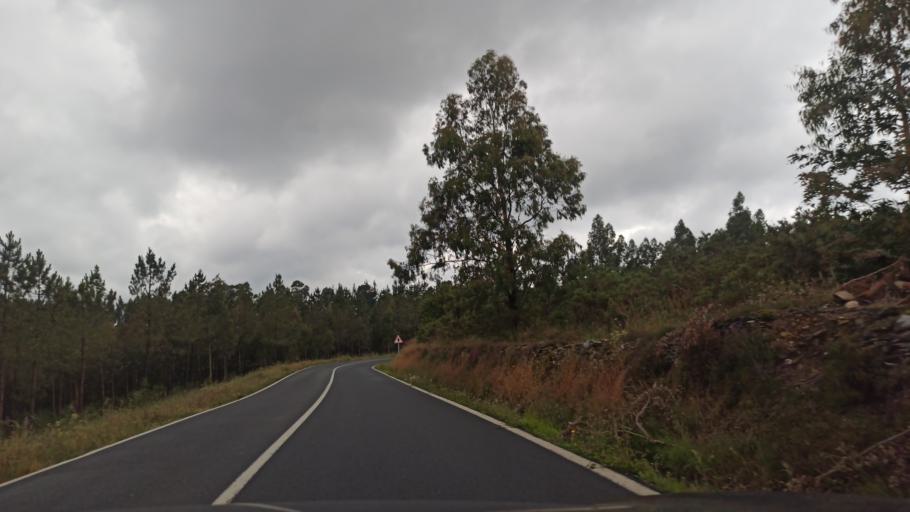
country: ES
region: Galicia
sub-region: Provincia da Coruna
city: Santiso
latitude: 42.7841
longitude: -8.0702
